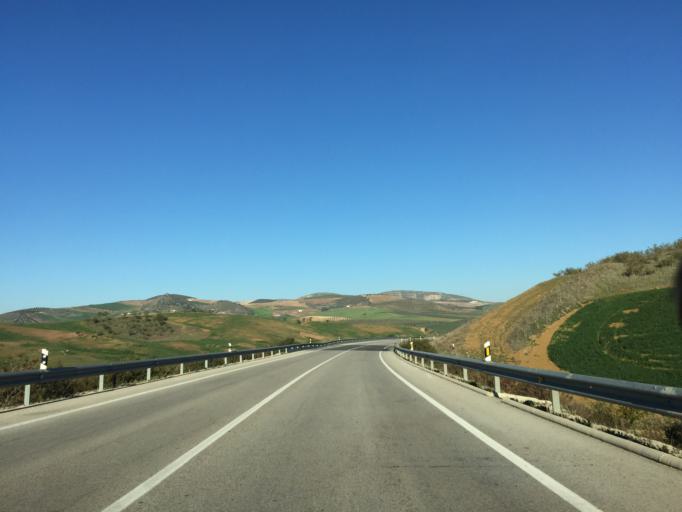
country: ES
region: Andalusia
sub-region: Provincia de Malaga
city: Teba
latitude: 36.9452
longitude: -4.8937
